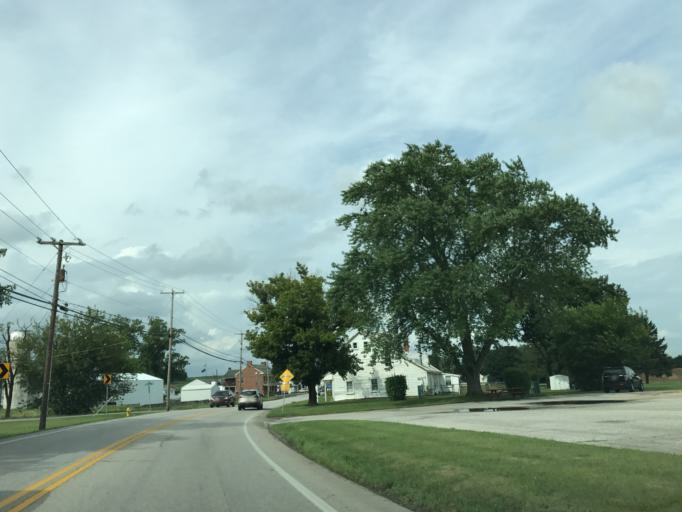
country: US
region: Pennsylvania
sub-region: York County
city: Spring Grove
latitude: 39.8962
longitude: -76.8565
